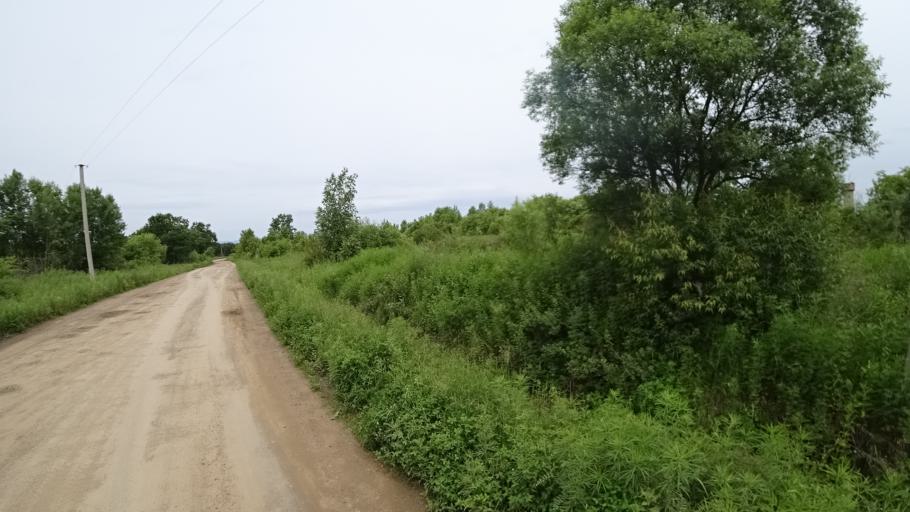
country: RU
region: Primorskiy
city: Arsen'yev
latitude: 44.1952
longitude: 133.3089
